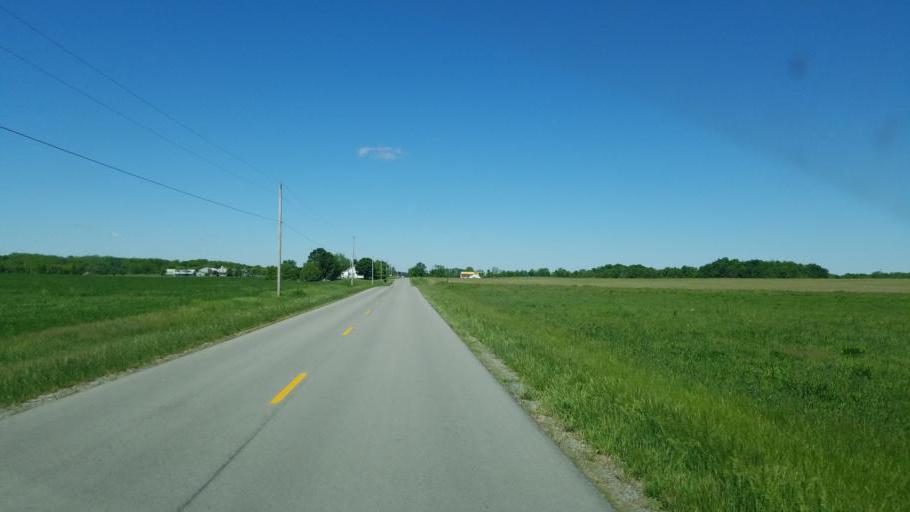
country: US
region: Ohio
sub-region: Logan County
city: Russells Point
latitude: 40.4249
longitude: -83.8631
